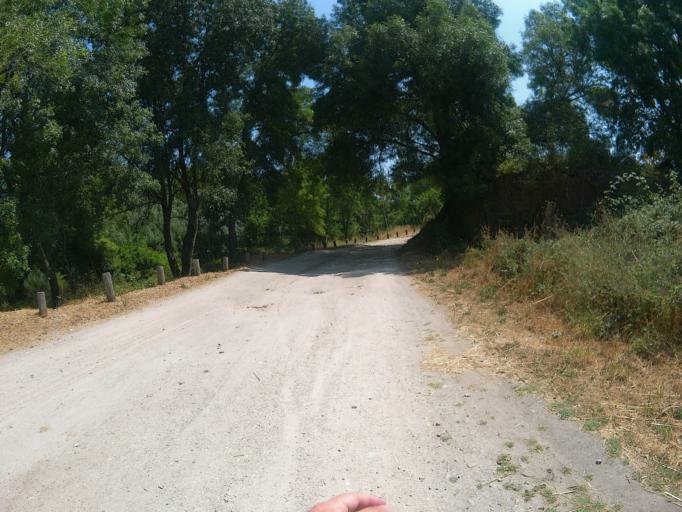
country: PT
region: Viana do Castelo
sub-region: Ponte de Lima
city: Ponte de Lima
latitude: 41.7770
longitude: -8.5740
